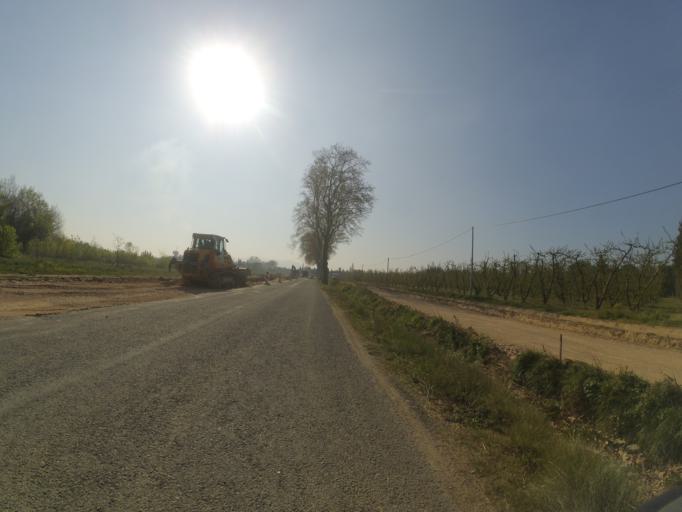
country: FR
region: Languedoc-Roussillon
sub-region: Departement des Pyrenees-Orientales
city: Thuir
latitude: 42.6475
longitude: 2.7366
